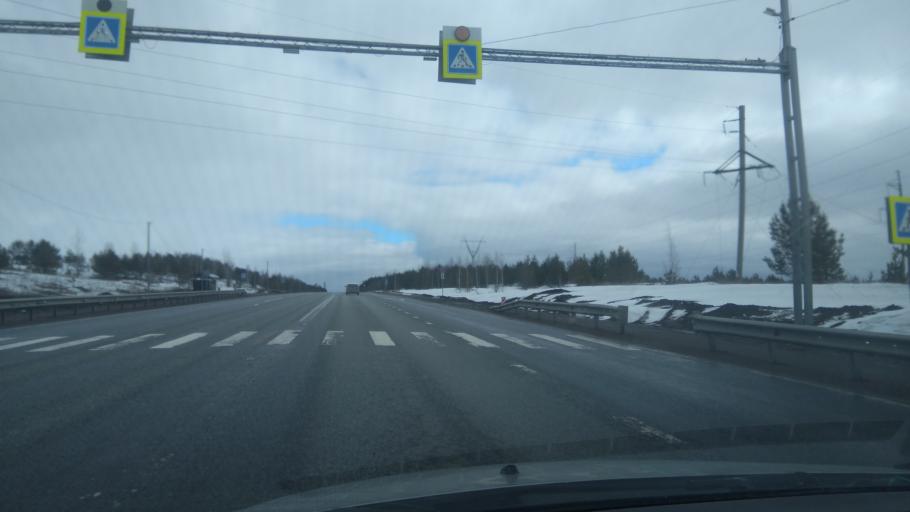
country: RU
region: Sverdlovsk
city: Achit
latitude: 56.7820
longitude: 57.9135
